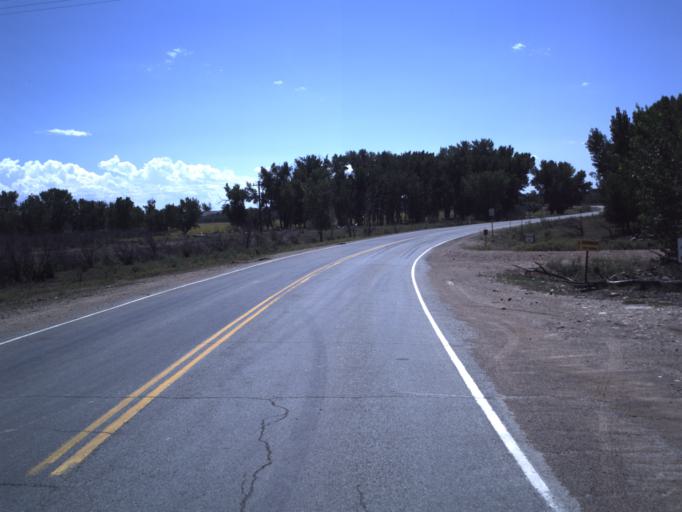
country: US
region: Utah
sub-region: Duchesne County
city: Roosevelt
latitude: 40.0841
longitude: -109.6758
